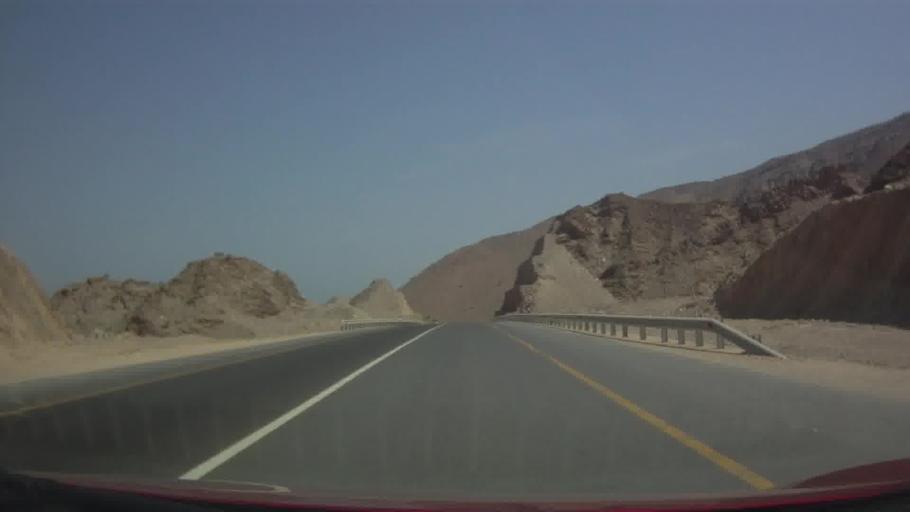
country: OM
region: Muhafazat Masqat
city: Muscat
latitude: 23.3939
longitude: 58.7885
